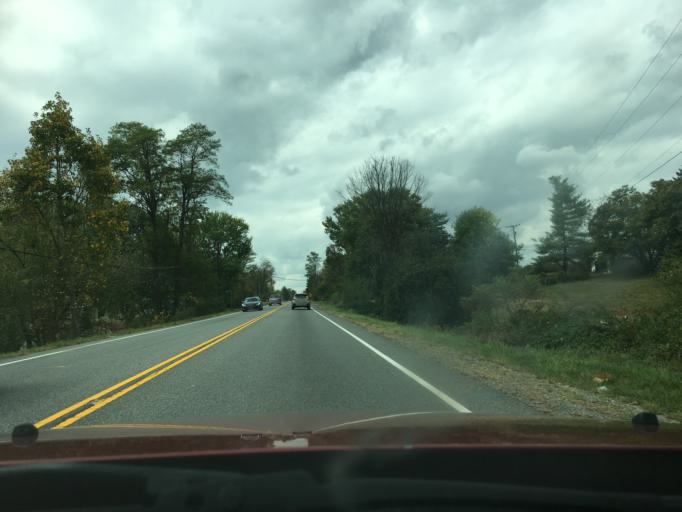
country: US
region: Virginia
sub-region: Montgomery County
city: Prices Fork
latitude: 37.1716
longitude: -80.5192
